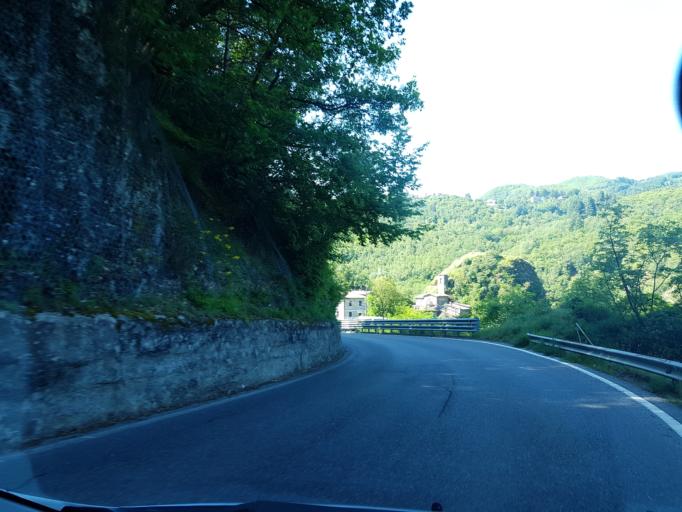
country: IT
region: Tuscany
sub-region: Provincia di Lucca
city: Piazza al Serchio-San Michele
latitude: 44.1763
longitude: 10.3126
